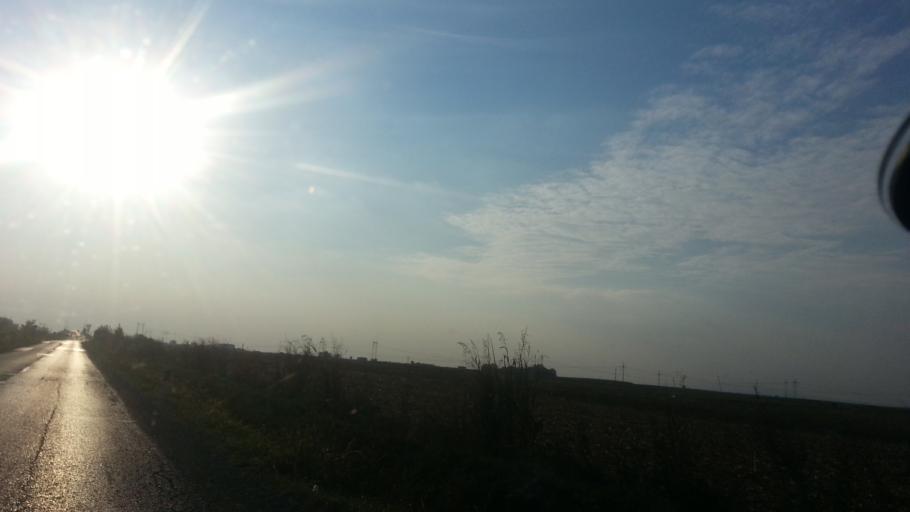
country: RS
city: Novi Karlovci
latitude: 45.0747
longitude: 20.1579
